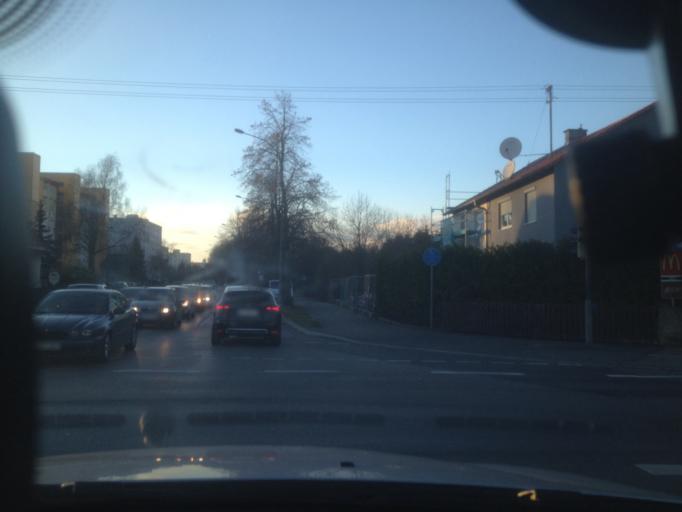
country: DE
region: Bavaria
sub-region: Swabia
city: Konigsbrunn
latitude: 48.2810
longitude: 10.8931
